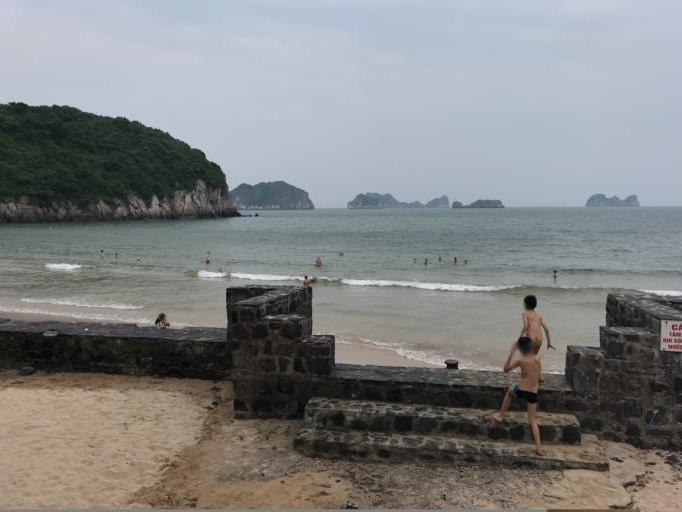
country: VN
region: Hai Phong
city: Cat Ba
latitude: 20.7176
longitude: 107.0522
